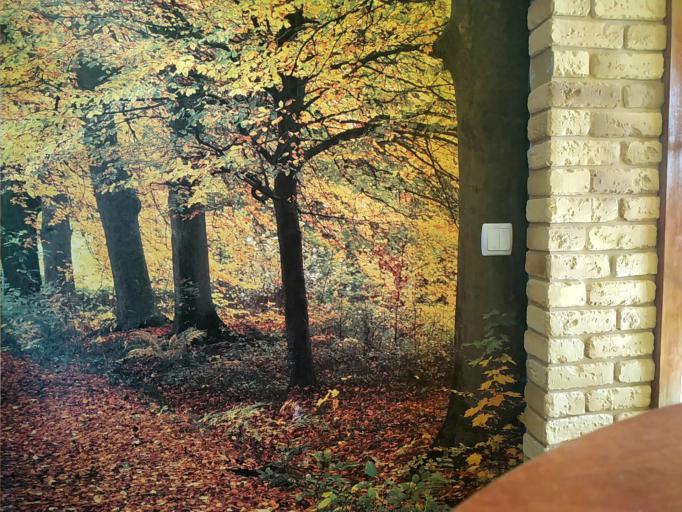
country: RU
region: Jaroslavl
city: Kukoboy
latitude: 58.8542
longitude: 39.7346
